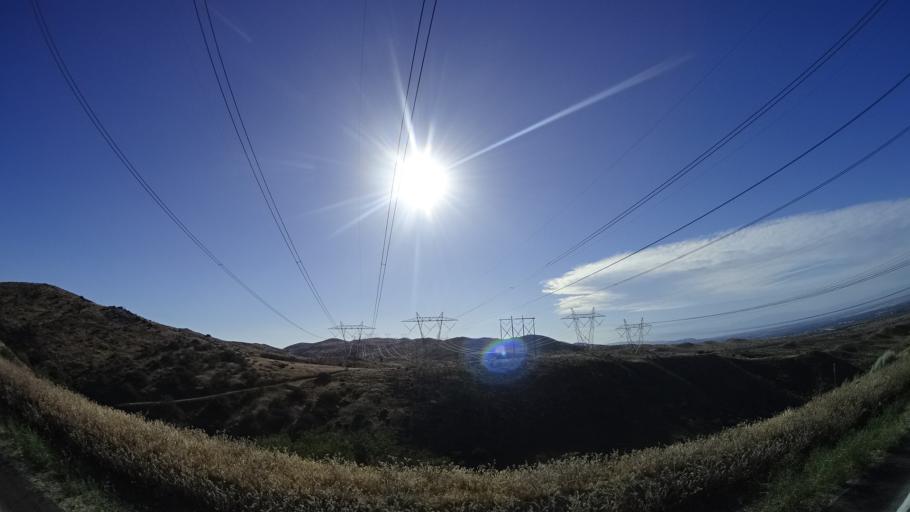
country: US
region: California
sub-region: Los Angeles County
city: Vincent
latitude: 34.4998
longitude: -118.0611
